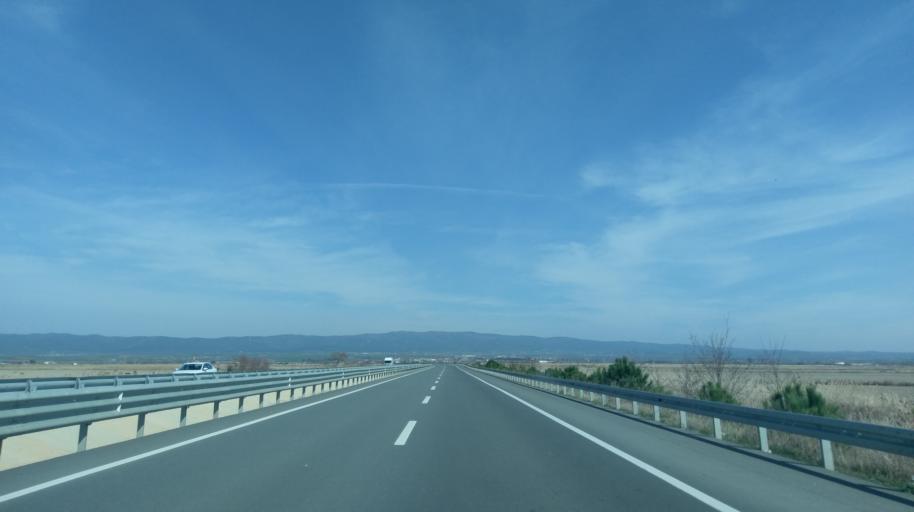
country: TR
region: Canakkale
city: Evrese
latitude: 40.6262
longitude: 26.8691
